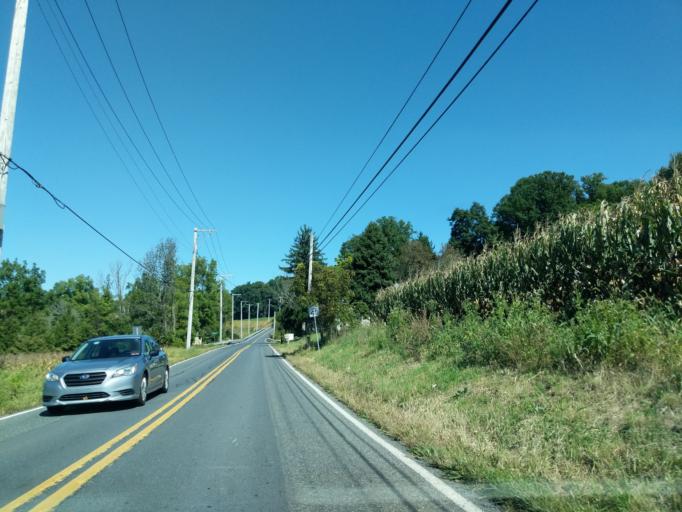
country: US
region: Pennsylvania
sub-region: Bucks County
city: Spinnerstown
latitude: 40.4826
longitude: -75.4593
